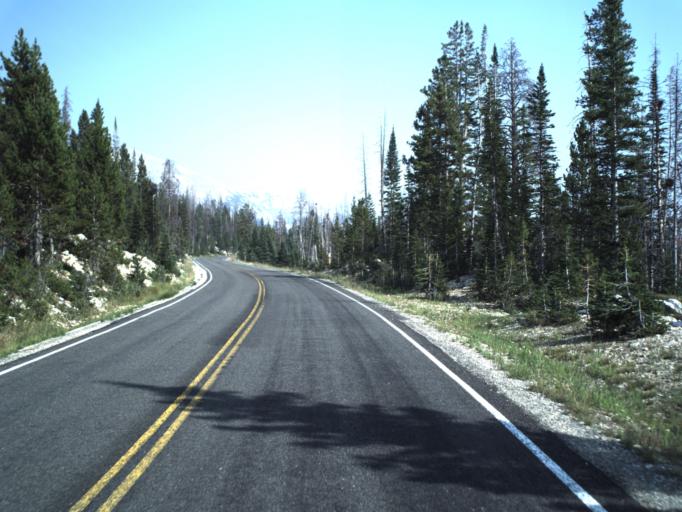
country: US
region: Utah
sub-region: Summit County
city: Kamas
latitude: 40.7130
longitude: -110.8883
